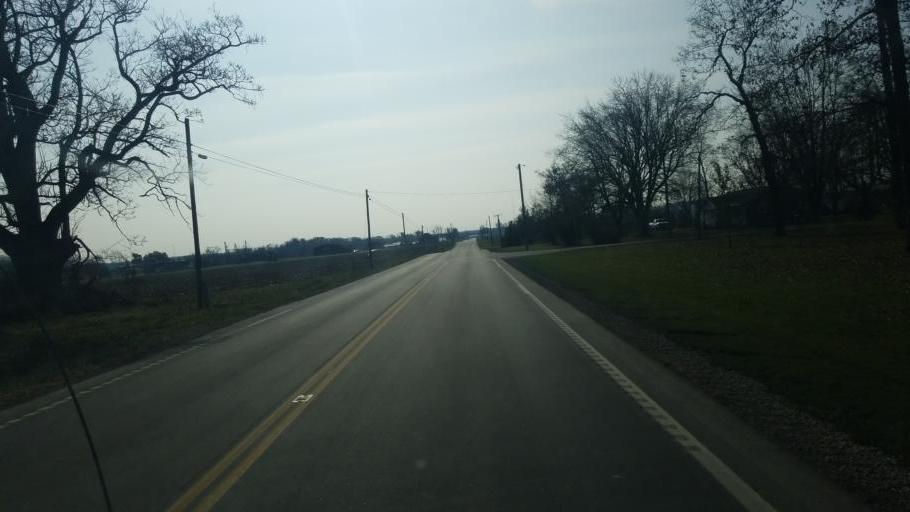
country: US
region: Ohio
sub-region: Mercer County
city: Fort Recovery
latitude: 40.4327
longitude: -84.7847
